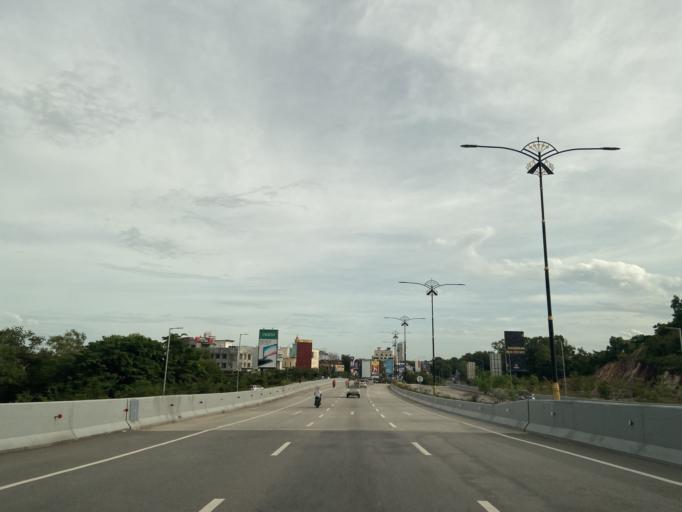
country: SG
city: Singapore
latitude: 1.1242
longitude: 104.0183
